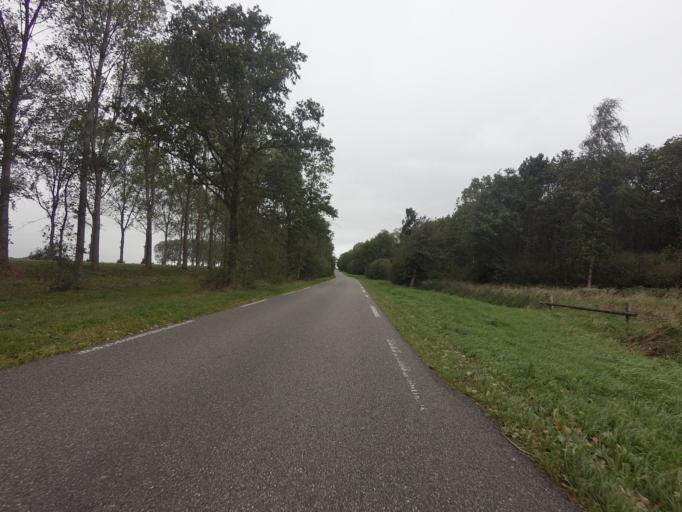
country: NL
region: Friesland
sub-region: Gemeente Opsterland
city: Tijnje
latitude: 53.0200
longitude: 6.0169
